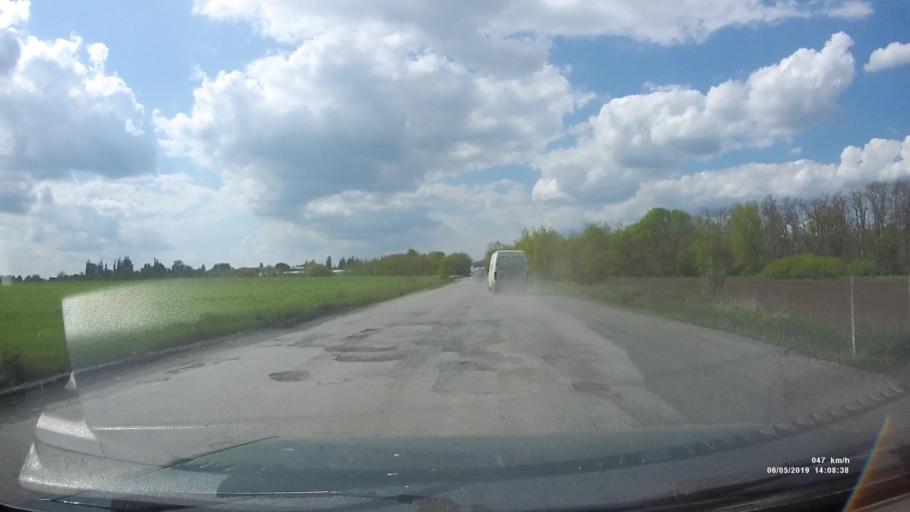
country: RU
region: Rostov
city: Shakhty
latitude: 47.6839
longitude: 40.2966
